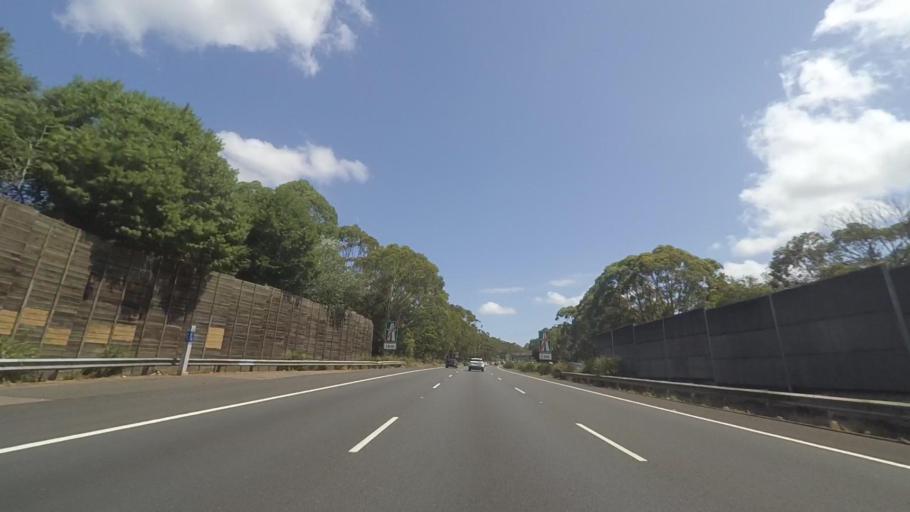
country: AU
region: New South Wales
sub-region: Ku-ring-gai
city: North Wahroonga
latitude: -33.7038
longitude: 151.1182
